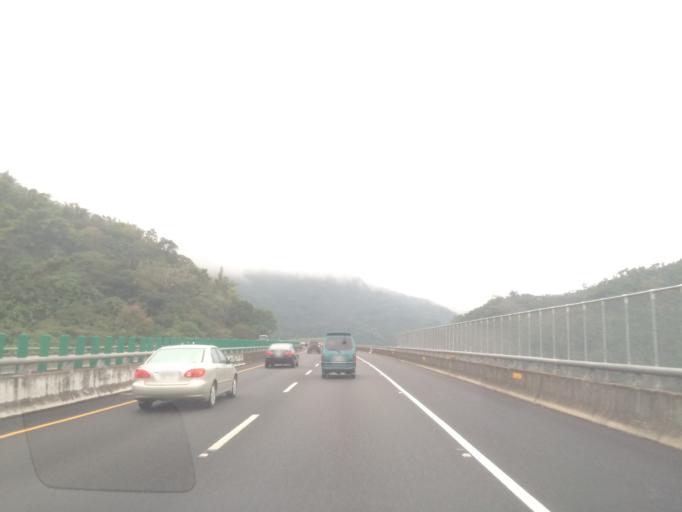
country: TW
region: Taiwan
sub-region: Nantou
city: Puli
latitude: 23.9935
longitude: 120.8531
